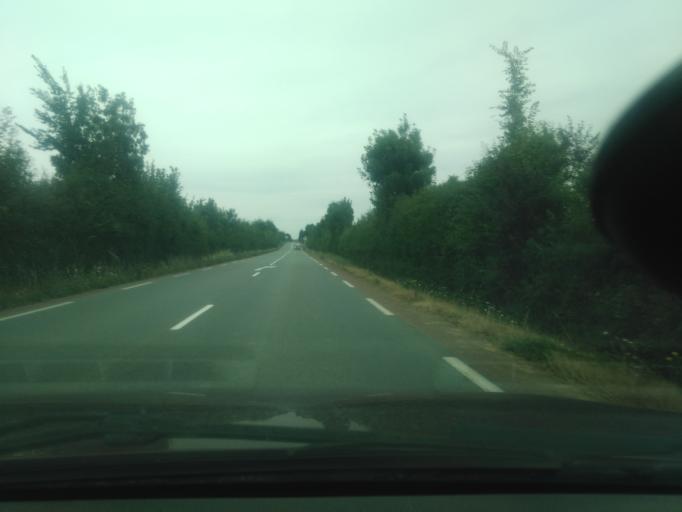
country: FR
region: Pays de la Loire
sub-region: Departement de la Vendee
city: Saint-Germain-de-Princay
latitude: 46.6826
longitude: -1.0101
